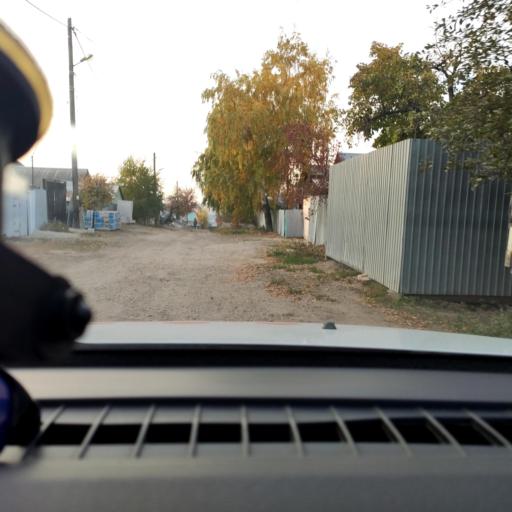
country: RU
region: Samara
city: Samara
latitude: 53.1840
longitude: 50.1968
